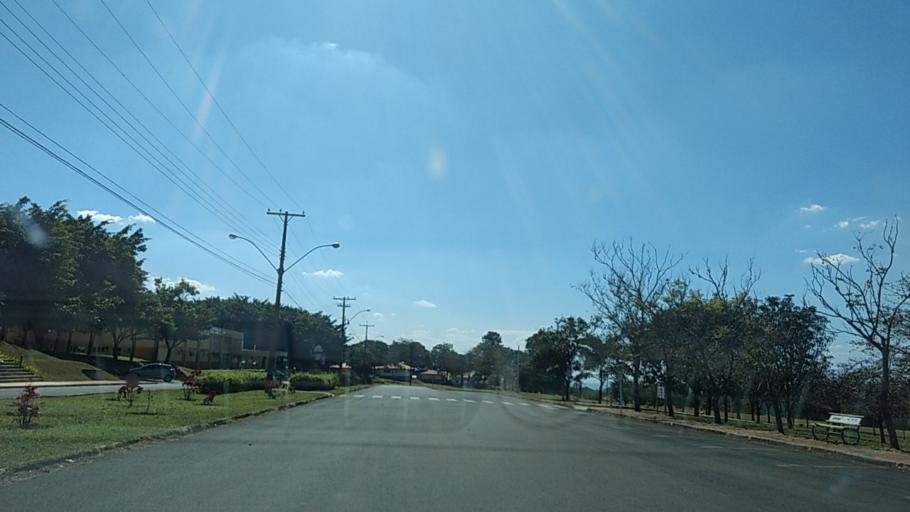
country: BR
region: Sao Paulo
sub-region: Botucatu
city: Botucatu
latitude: -22.8480
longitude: -48.4340
